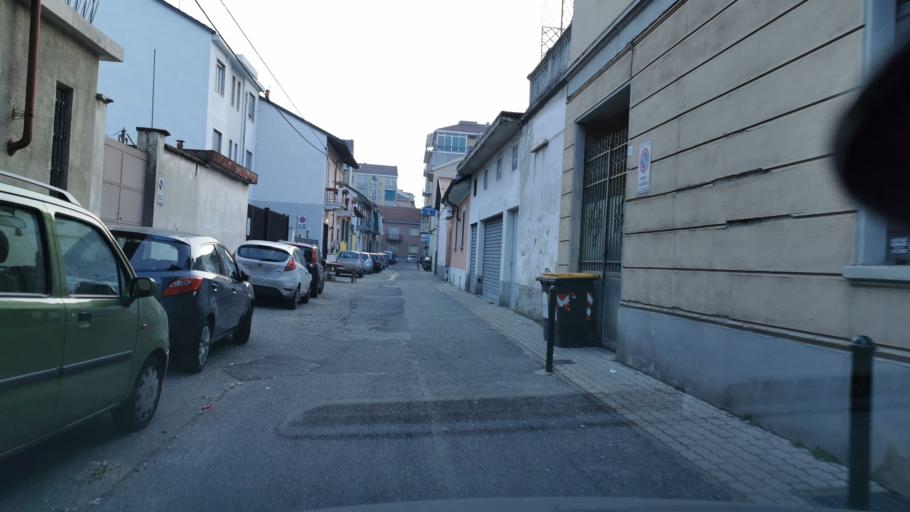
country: IT
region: Piedmont
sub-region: Provincia di Torino
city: Venaria Reale
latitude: 45.1006
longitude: 7.6593
